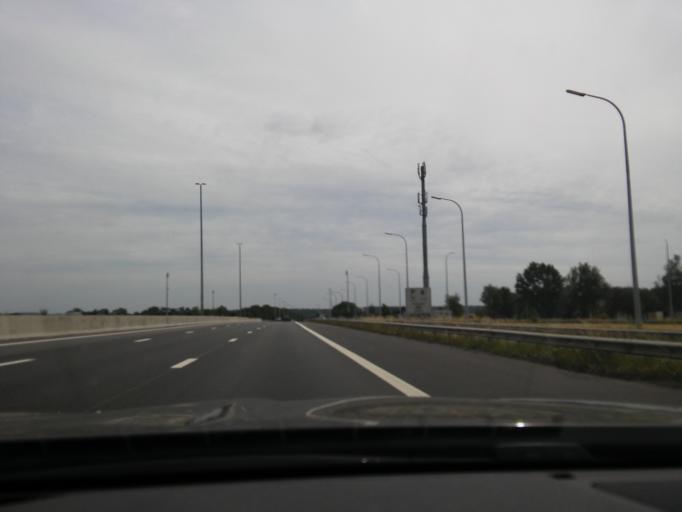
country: BE
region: Flanders
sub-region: Provincie Vlaams-Brabant
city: Bertem
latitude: 50.8574
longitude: 4.6375
